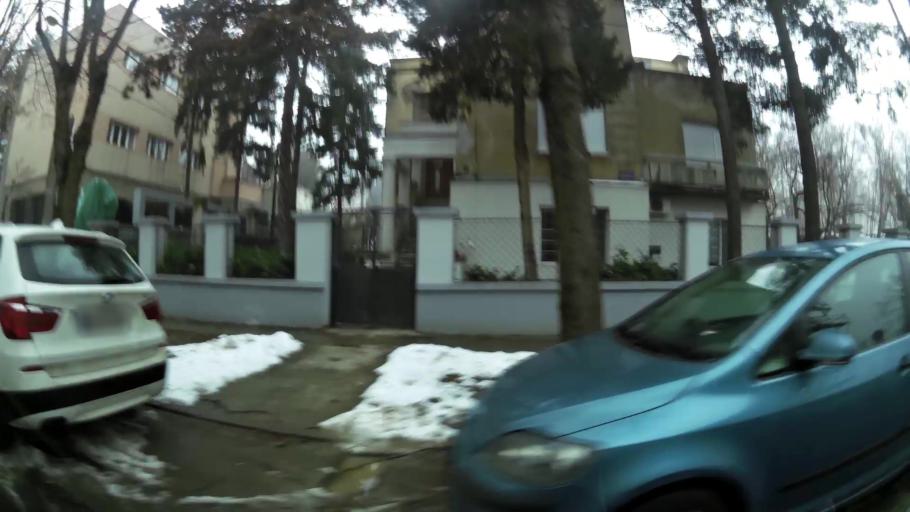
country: RS
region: Central Serbia
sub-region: Belgrade
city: Savski Venac
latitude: 44.7854
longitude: 20.4396
